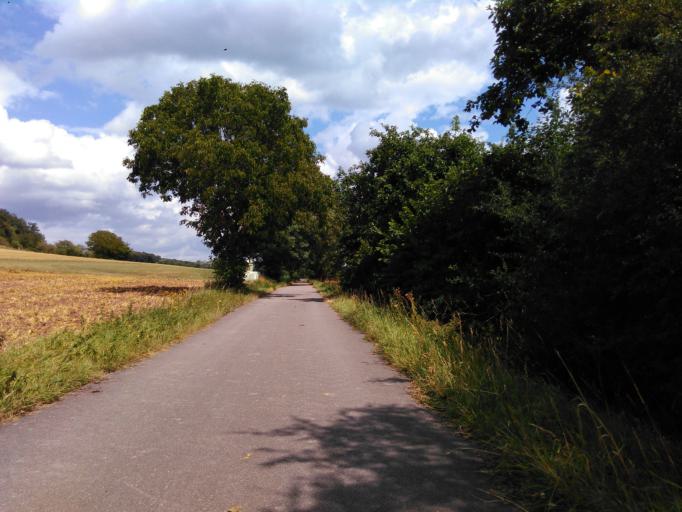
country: LU
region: Grevenmacher
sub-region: Canton d'Echternach
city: Consdorf
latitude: 49.7409
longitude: 6.3244
